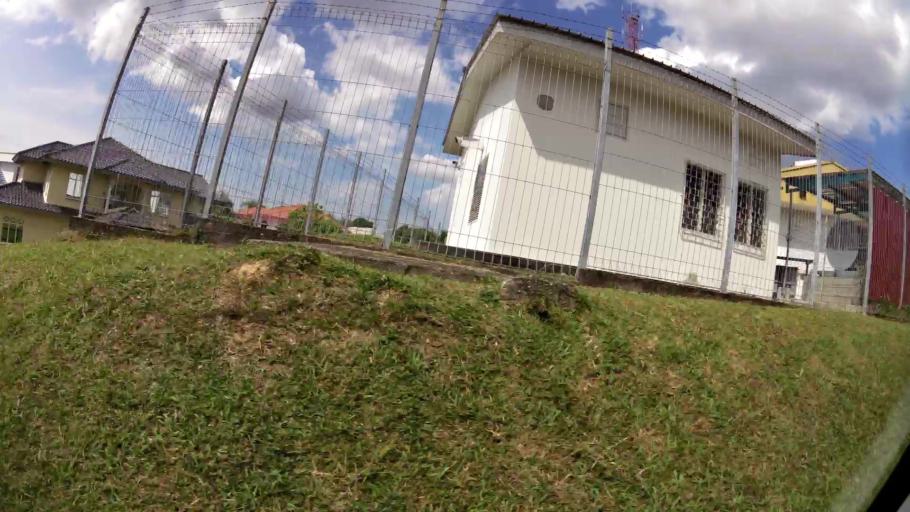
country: BN
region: Brunei and Muara
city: Bandar Seri Begawan
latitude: 4.9573
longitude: 114.9547
